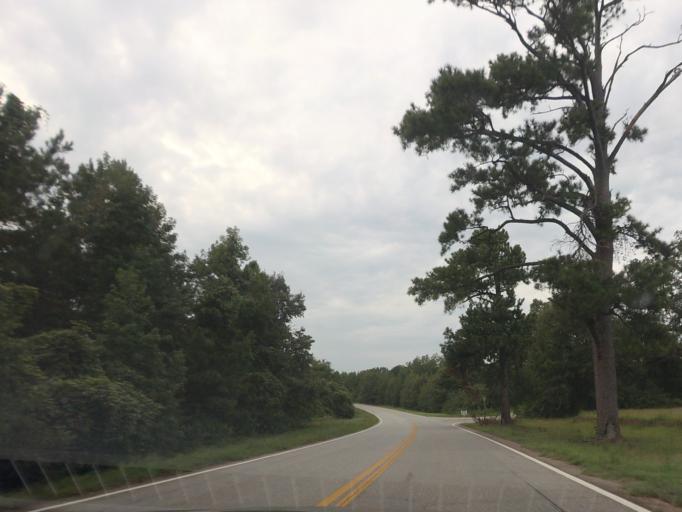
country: US
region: Georgia
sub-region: Twiggs County
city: Jeffersonville
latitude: 32.7446
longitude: -83.4270
